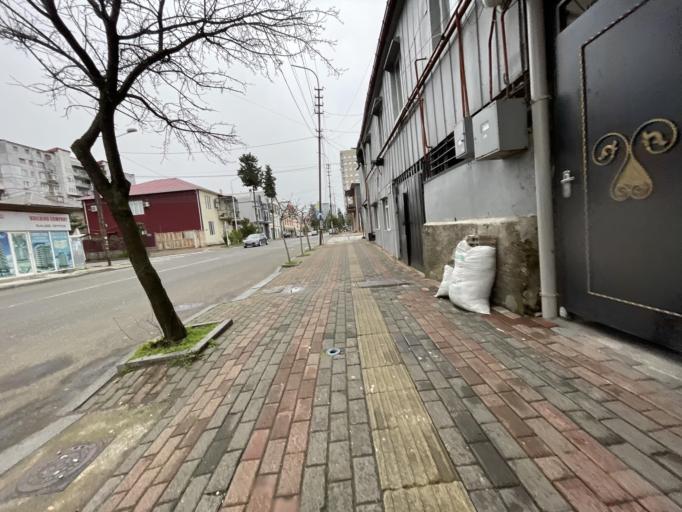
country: GE
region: Ajaria
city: Batumi
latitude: 41.6398
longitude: 41.6416
